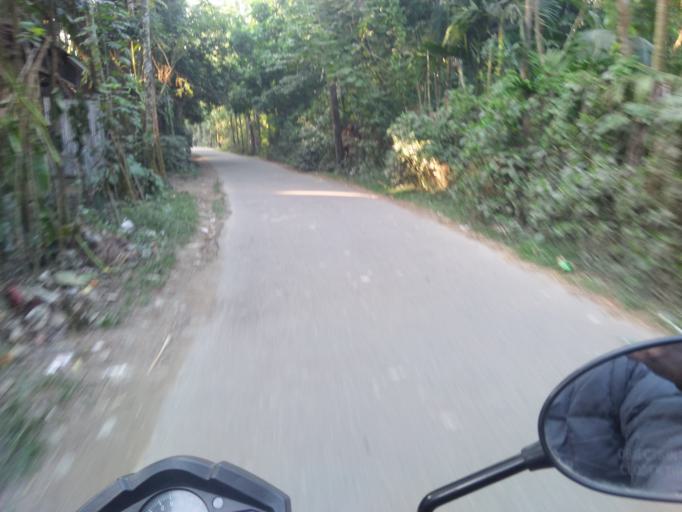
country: BD
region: Barisal
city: Bhola
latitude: 22.7518
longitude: 90.6341
